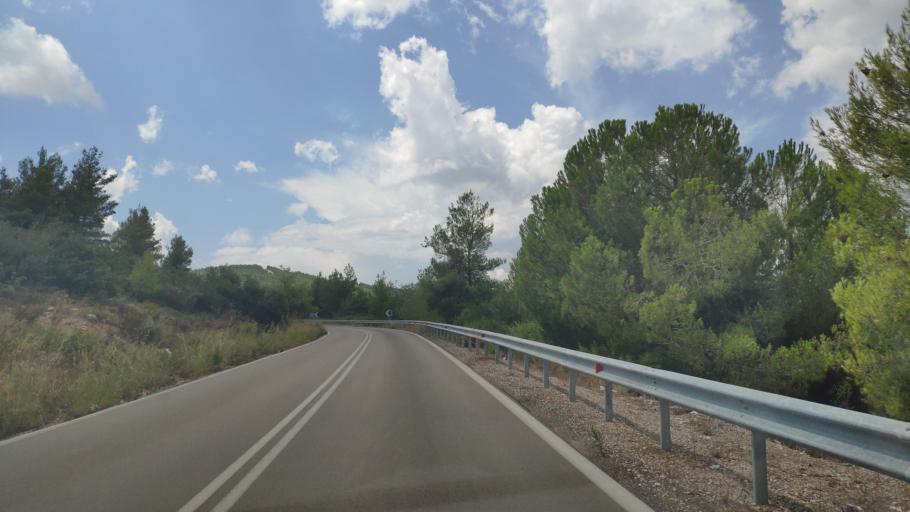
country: GR
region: Central Greece
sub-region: Nomos Fthiotidos
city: Martinon
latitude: 38.6083
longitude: 23.1792
